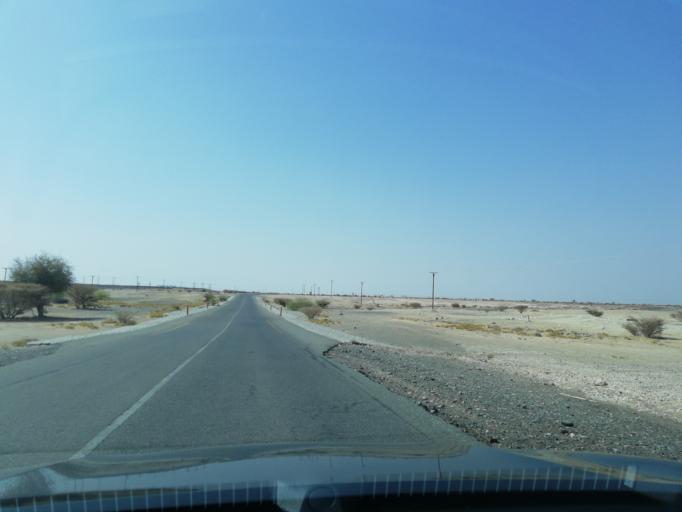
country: OM
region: Muhafazat ad Dakhiliyah
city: Adam
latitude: 22.3572
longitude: 58.0668
